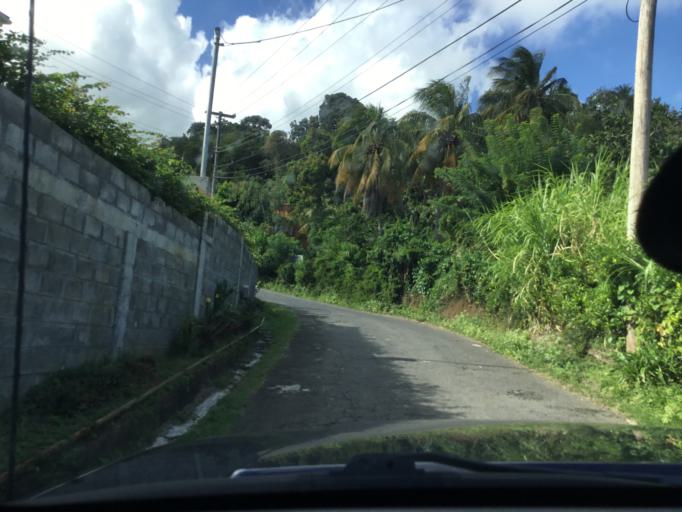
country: VC
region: Saint George
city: Kingstown
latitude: 13.1482
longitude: -61.1754
